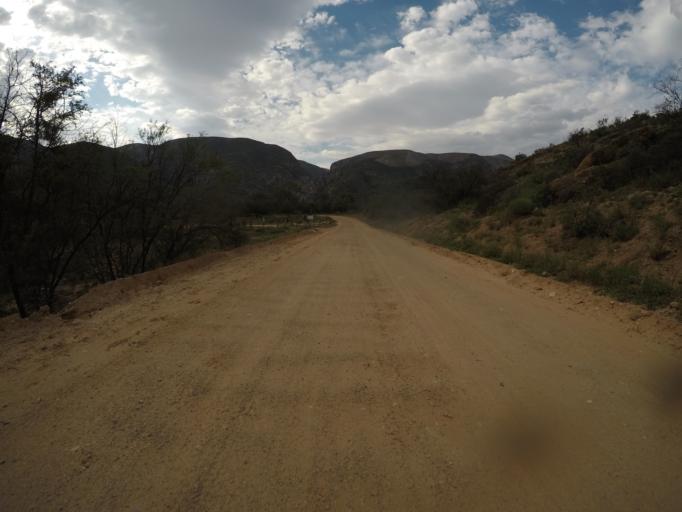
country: ZA
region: Eastern Cape
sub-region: Cacadu District Municipality
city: Kareedouw
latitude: -33.5850
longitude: 24.1653
